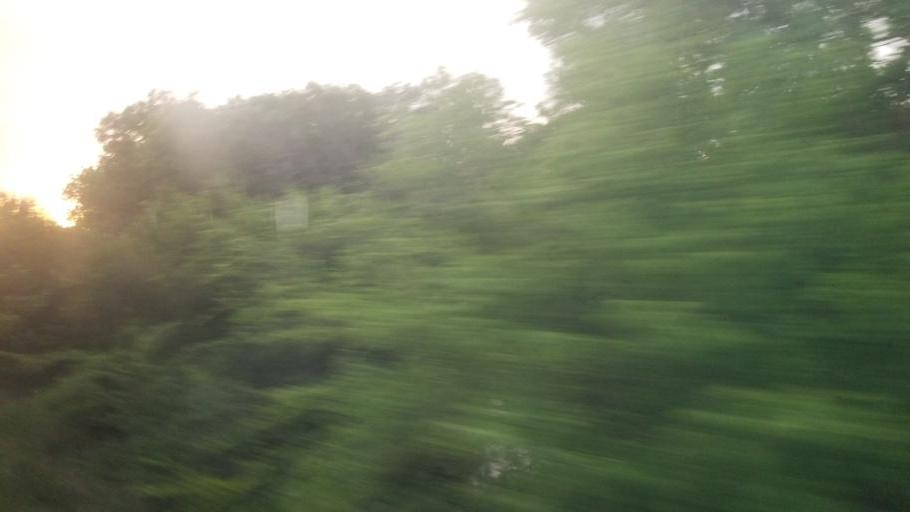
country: US
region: Kansas
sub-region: Marion County
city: Peabody
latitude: 38.1587
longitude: -97.1151
